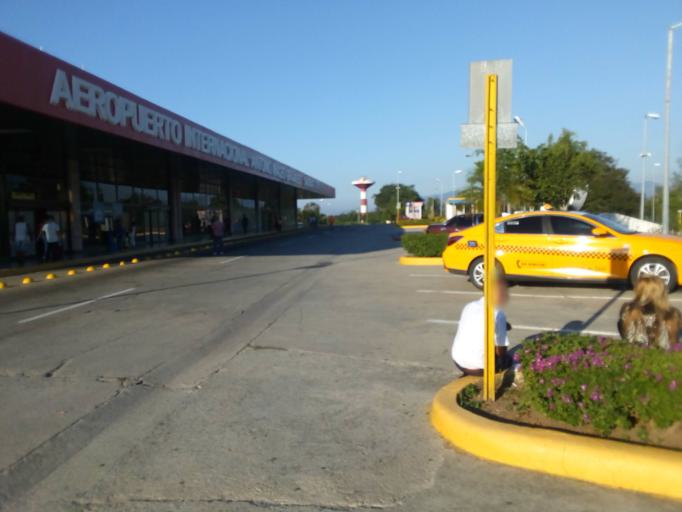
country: CU
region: Santiago de Cuba
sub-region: Municipio de Santiago de Cuba
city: Santiago de Cuba
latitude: 19.9727
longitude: -75.8395
